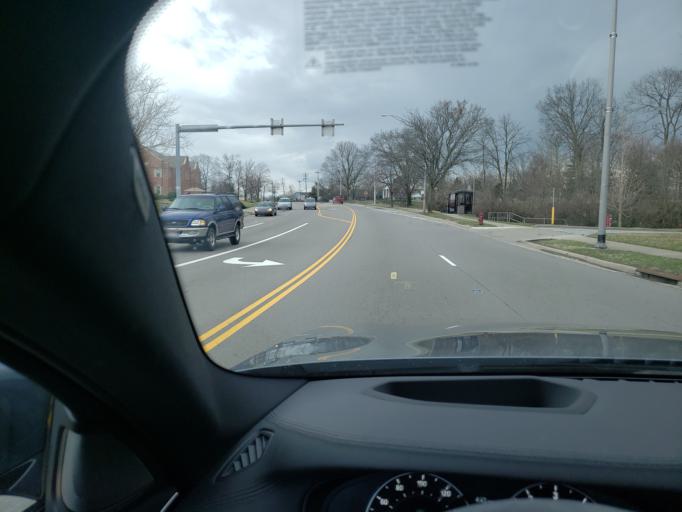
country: US
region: Ohio
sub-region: Hamilton County
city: Springdale
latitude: 39.2820
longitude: -84.4854
